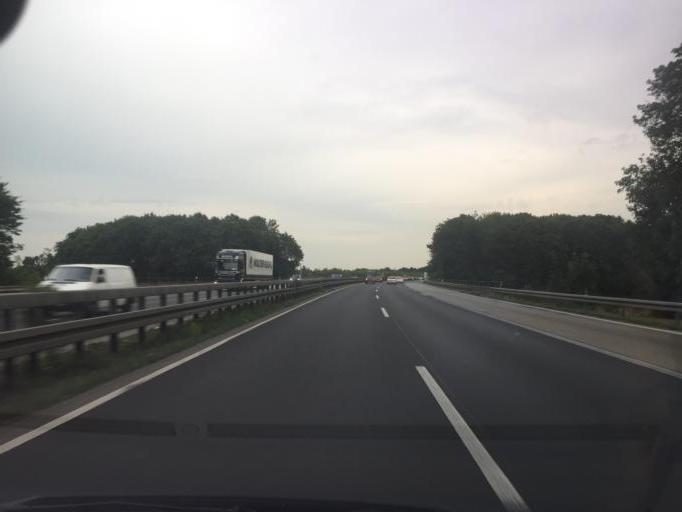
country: DE
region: North Rhine-Westphalia
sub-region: Regierungsbezirk Dusseldorf
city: Viersen
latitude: 51.2116
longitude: 6.3784
